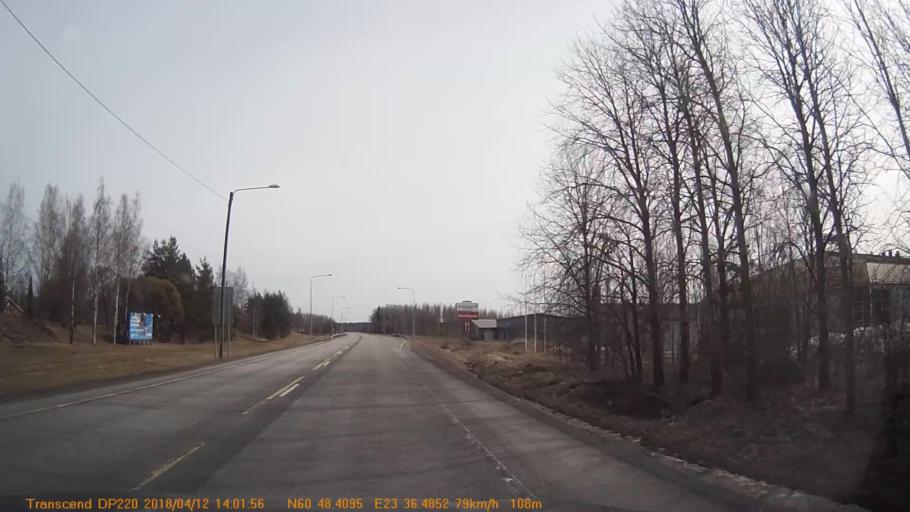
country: FI
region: Haeme
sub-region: Forssa
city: Forssa
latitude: 60.8067
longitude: 23.6083
